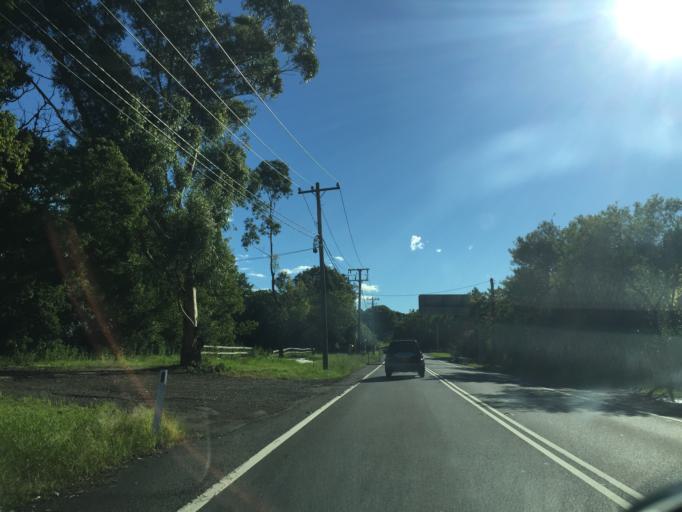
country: AU
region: New South Wales
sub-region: Hornsby Shire
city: Galston
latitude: -33.6530
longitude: 151.0420
